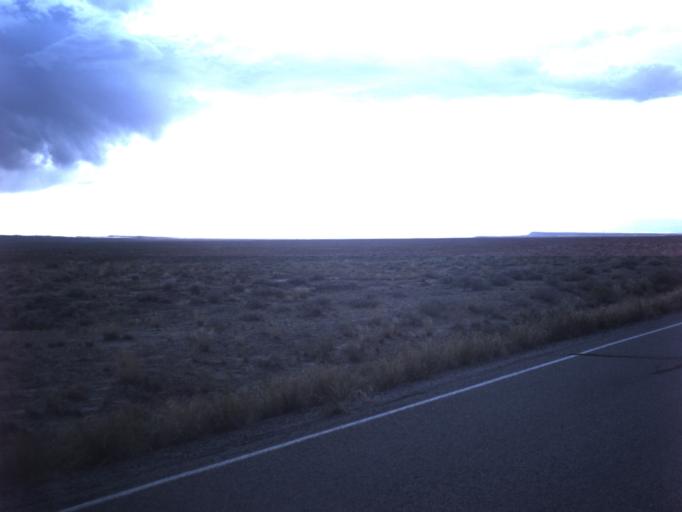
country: US
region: Utah
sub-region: Grand County
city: Moab
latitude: 38.9161
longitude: -109.3296
